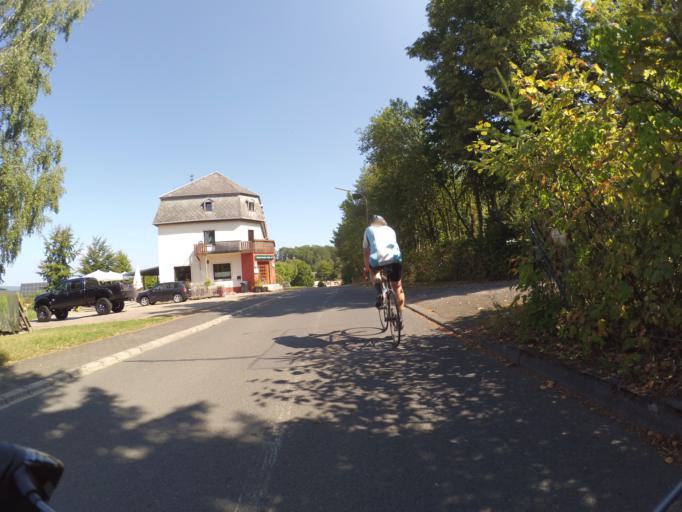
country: DE
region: Rheinland-Pfalz
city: Morbach
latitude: 49.7750
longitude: 7.1001
